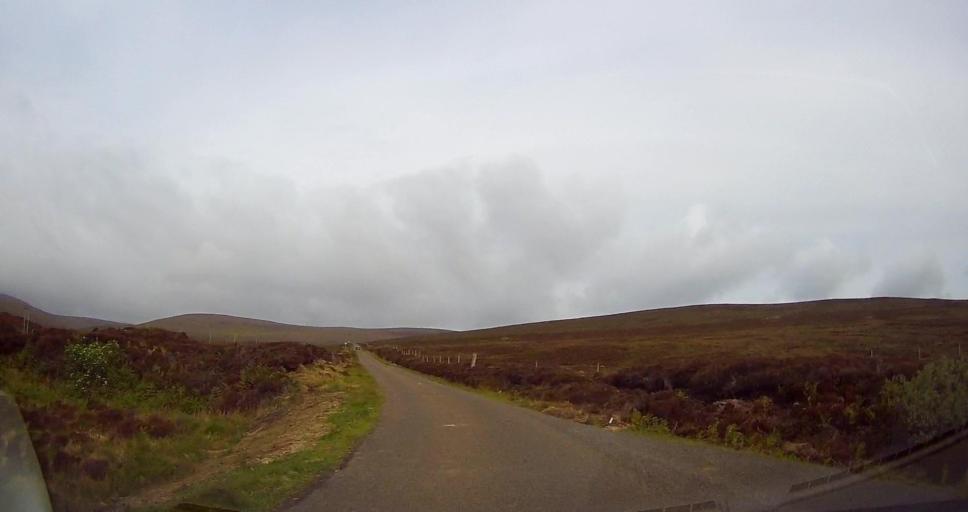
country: GB
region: Scotland
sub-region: Orkney Islands
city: Stromness
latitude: 58.8704
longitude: -3.2321
